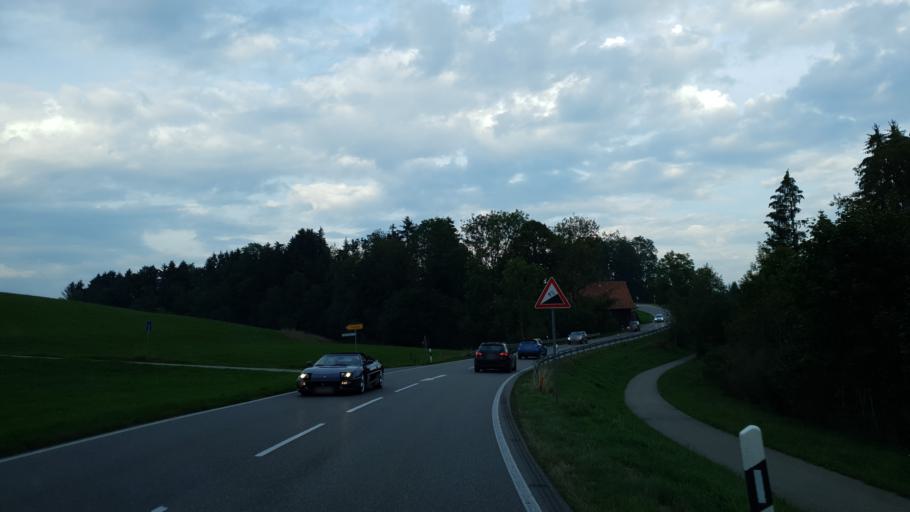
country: DE
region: Bavaria
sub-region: Swabia
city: Gestratz
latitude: 47.6650
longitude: 9.9428
